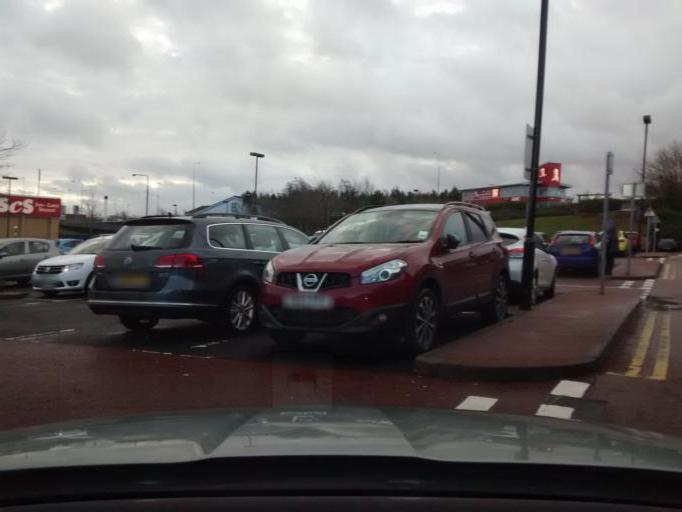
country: GB
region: Scotland
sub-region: West Lothian
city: Livingston
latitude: 55.8811
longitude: -3.5221
